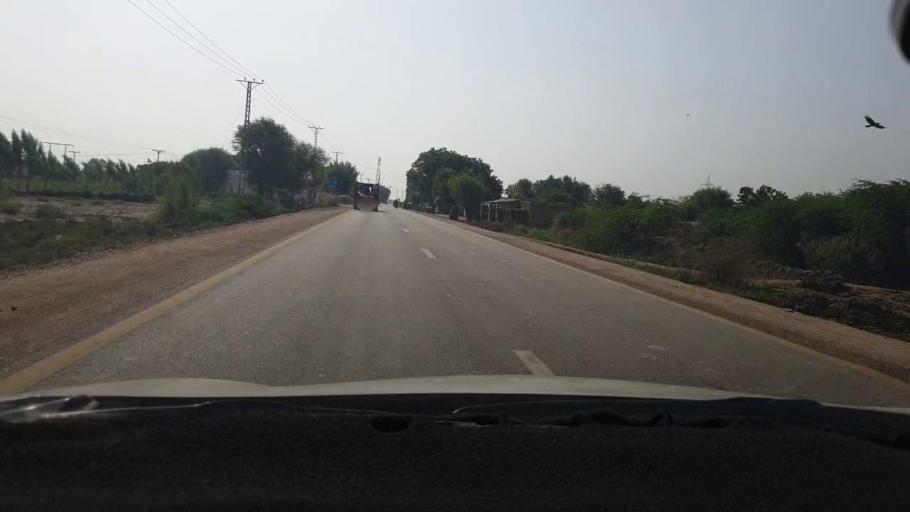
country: PK
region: Sindh
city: Jhol
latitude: 25.9435
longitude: 68.9852
